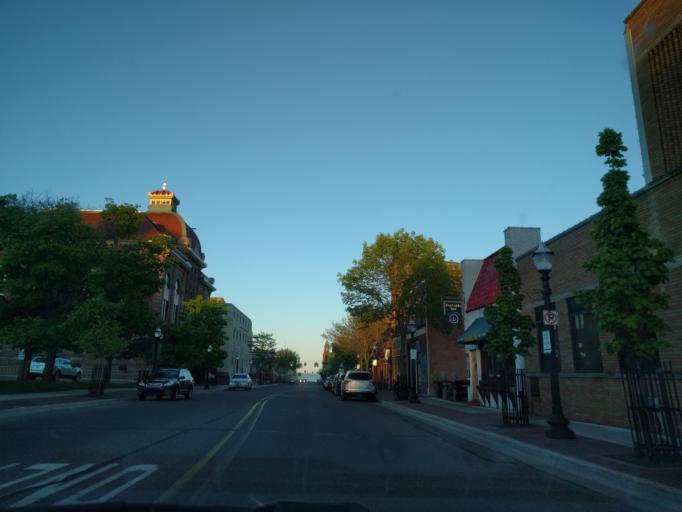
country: US
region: Michigan
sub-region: Marquette County
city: Marquette
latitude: 46.5439
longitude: -87.3973
